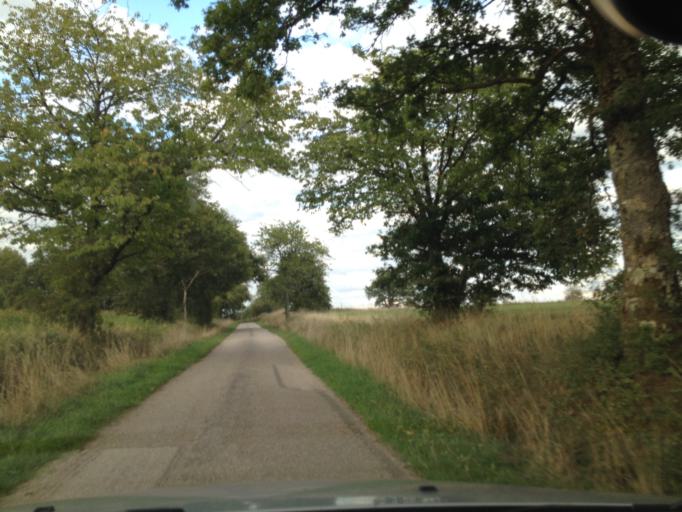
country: FR
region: Lorraine
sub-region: Departement des Vosges
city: Bains-les-Bains
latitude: 47.9853
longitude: 6.1893
